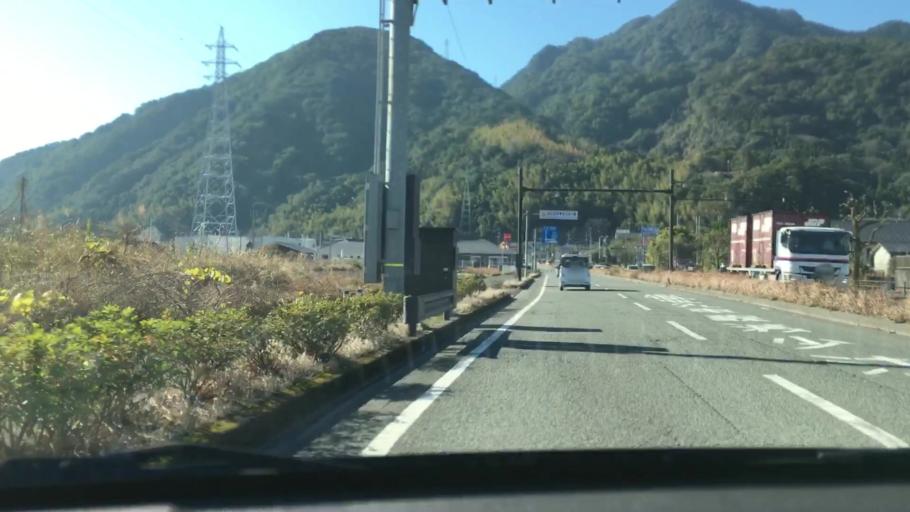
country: JP
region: Kagoshima
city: Kajiki
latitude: 31.7061
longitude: 130.6135
